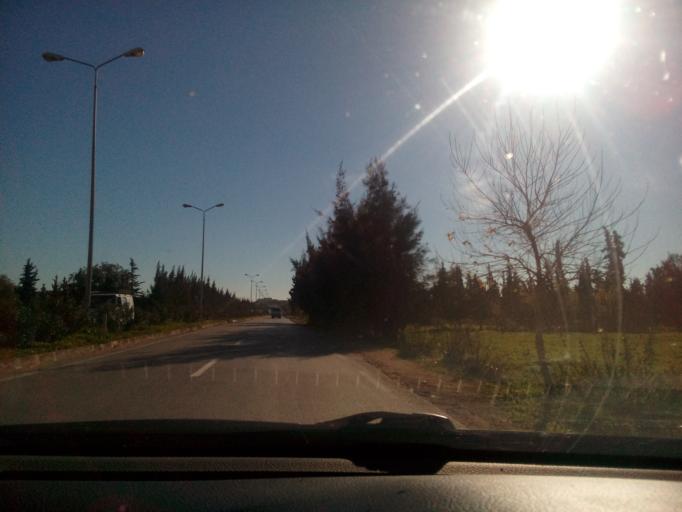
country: DZ
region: Relizane
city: Relizane
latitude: 35.7211
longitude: 0.5073
